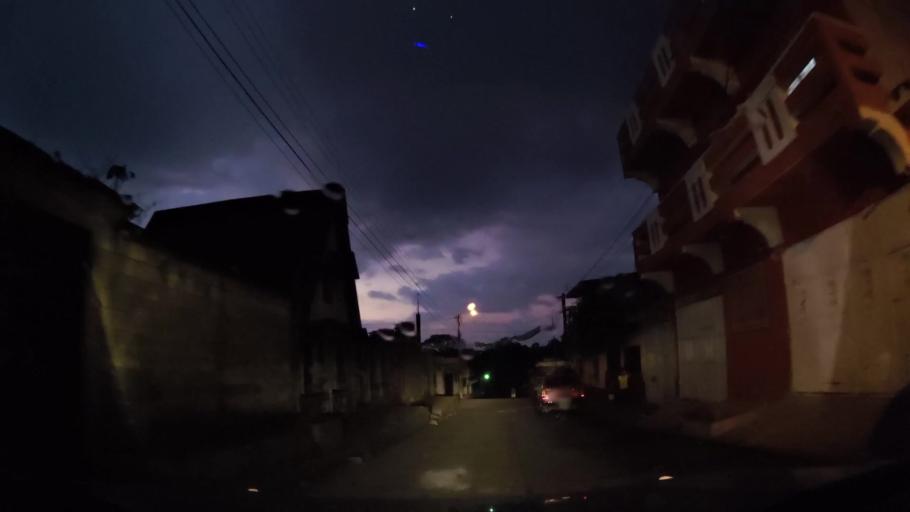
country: GT
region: Escuintla
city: Santa Lucia Cotzumalguapa
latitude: 14.3361
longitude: -91.0319
